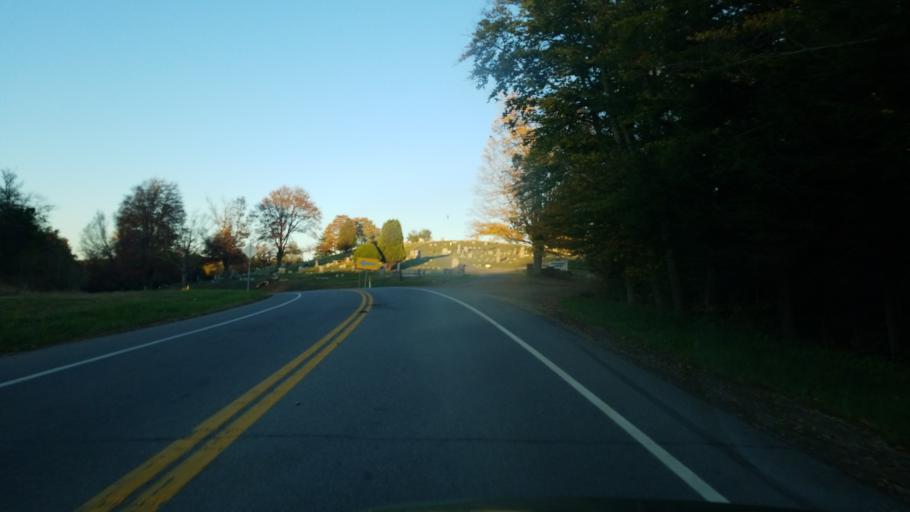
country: US
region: Pennsylvania
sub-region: Jefferson County
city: Reynoldsville
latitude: 41.0825
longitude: -78.8955
